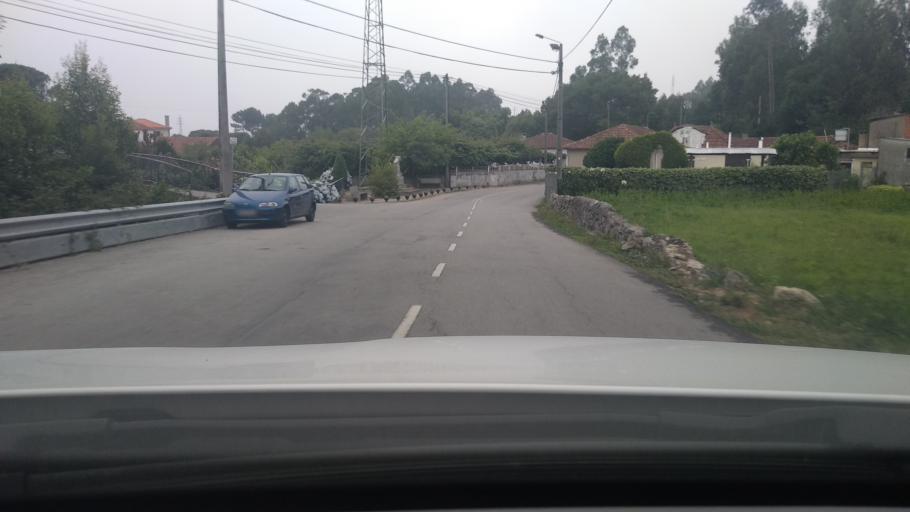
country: PT
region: Aveiro
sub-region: Espinho
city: Silvalde
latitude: 40.9972
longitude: -8.6278
